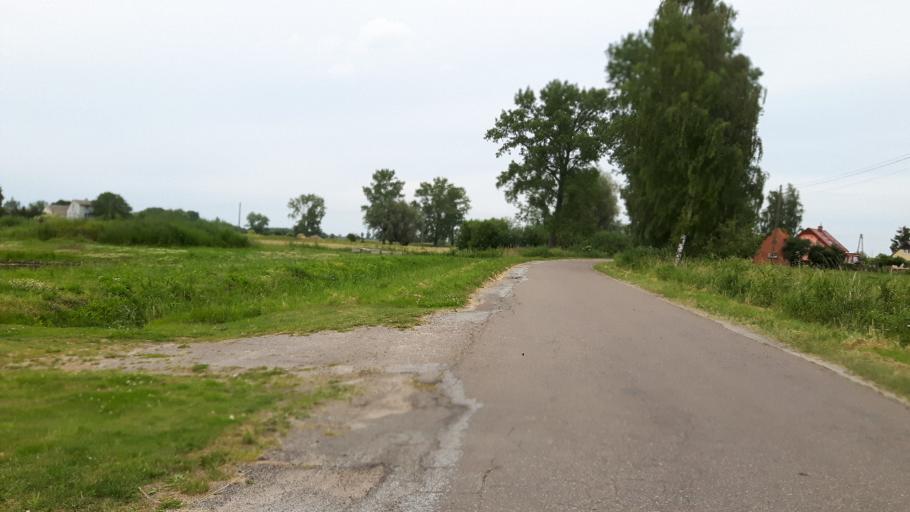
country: PL
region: Pomeranian Voivodeship
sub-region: Powiat nowodworski
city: Sztutowo
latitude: 54.2642
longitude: 19.1667
